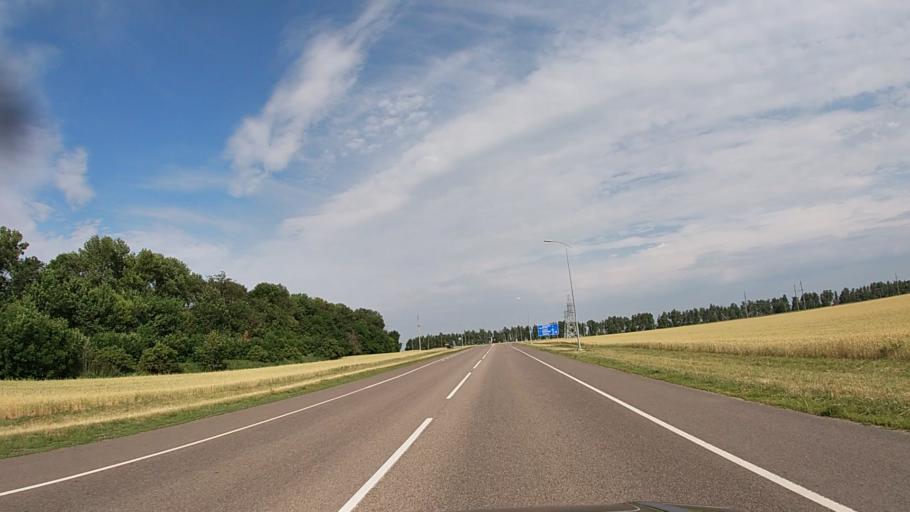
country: RU
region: Belgorod
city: Proletarskiy
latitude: 50.8297
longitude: 35.7709
